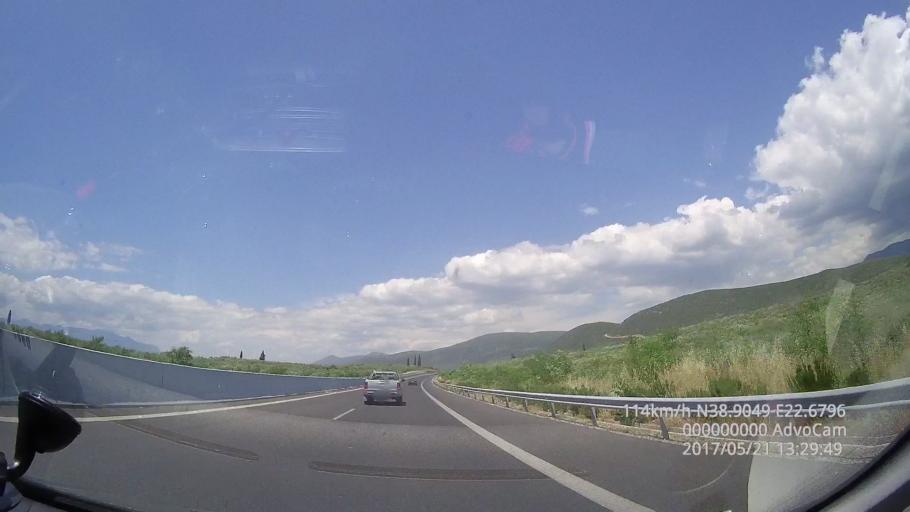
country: GR
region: Central Greece
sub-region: Nomos Fthiotidos
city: Stylida
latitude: 38.9049
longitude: 22.6791
